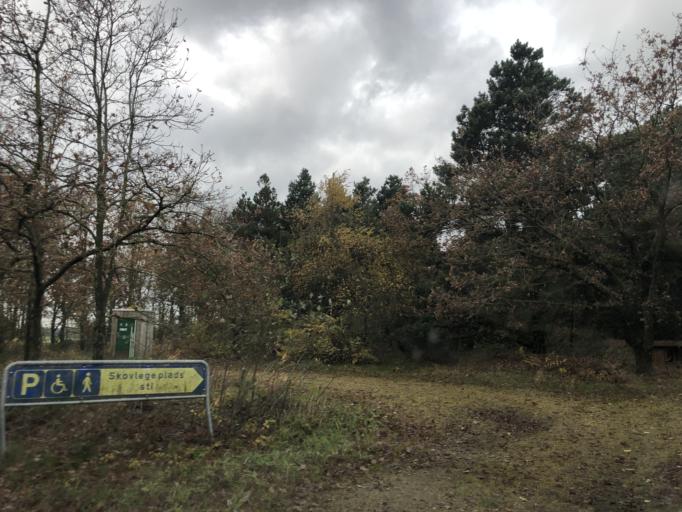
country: DK
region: Central Jutland
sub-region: Holstebro Kommune
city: Ulfborg
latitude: 56.3134
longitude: 8.2056
